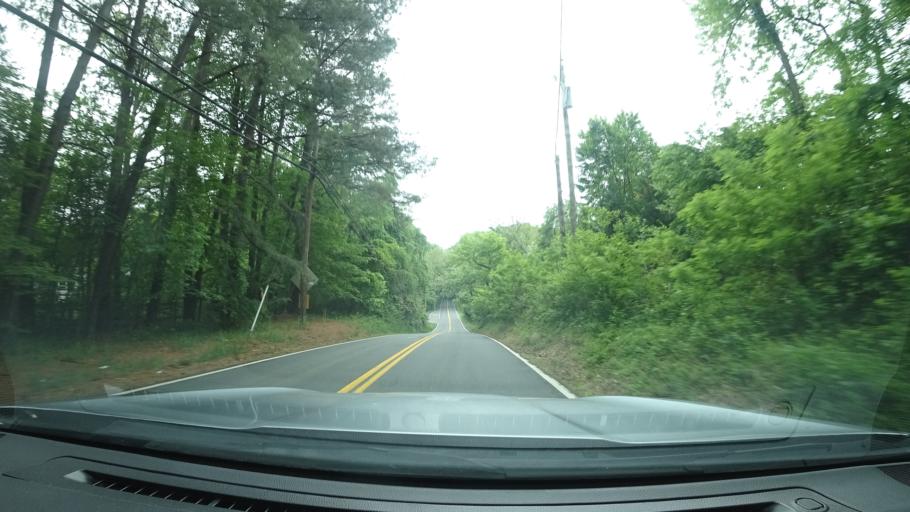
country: US
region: Virginia
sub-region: Fairfax County
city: Oakton
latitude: 38.8948
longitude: -77.3510
